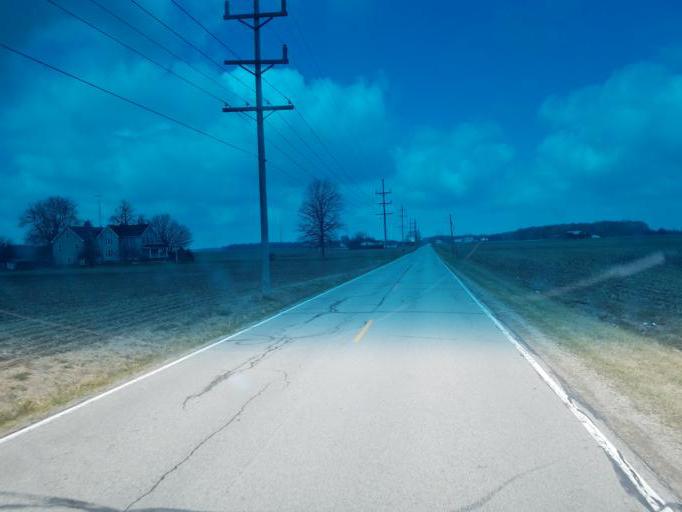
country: US
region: Ohio
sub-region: Crawford County
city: Galion
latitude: 40.7848
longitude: -82.8246
